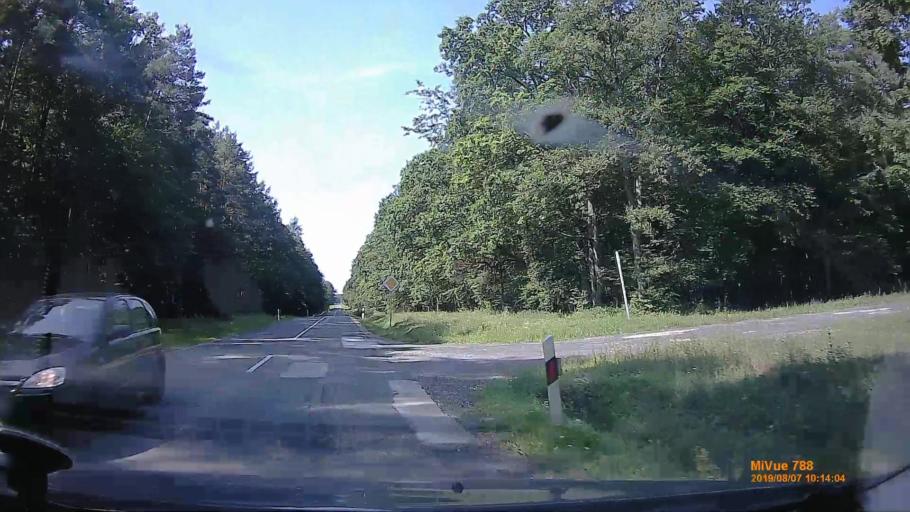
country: HU
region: Zala
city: Lenti
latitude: 46.6601
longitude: 16.6331
